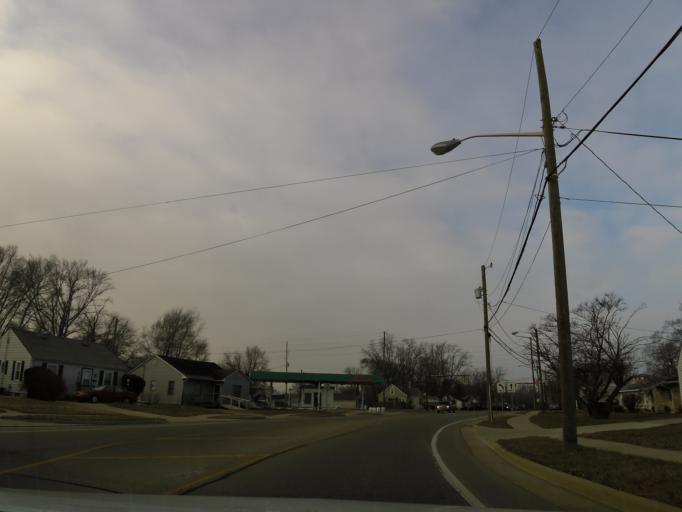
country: US
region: Indiana
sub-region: Bartholomew County
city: Columbus
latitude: 39.2162
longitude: -85.8885
